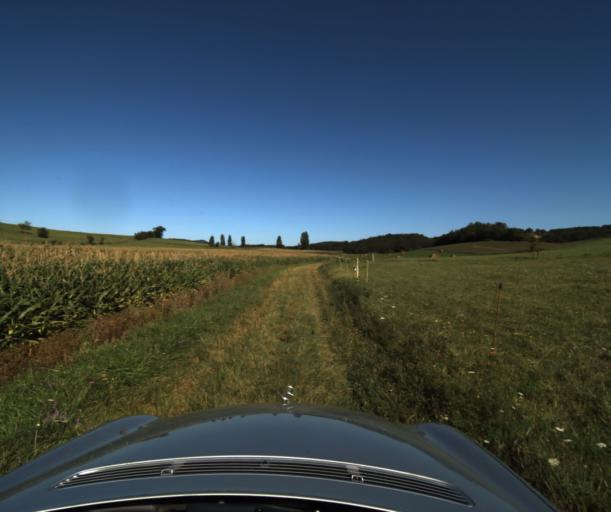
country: FR
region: Midi-Pyrenees
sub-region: Departement de l'Ariege
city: Lavelanet
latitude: 42.9812
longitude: 1.9080
